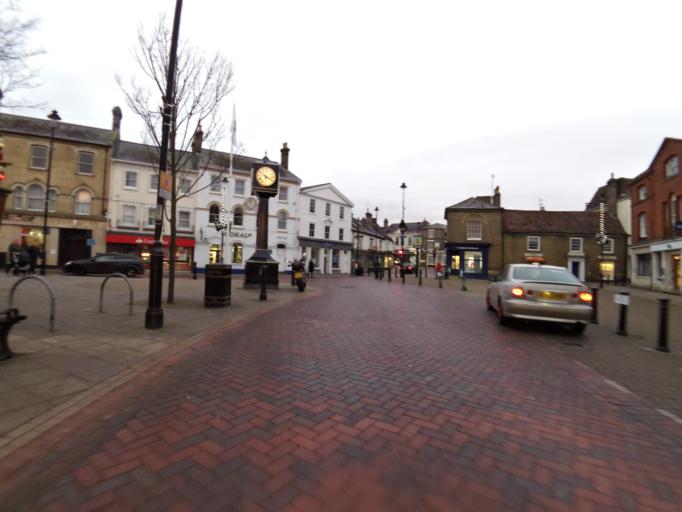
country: GB
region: England
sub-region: Suffolk
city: Stowmarket
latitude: 52.1876
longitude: 0.9956
